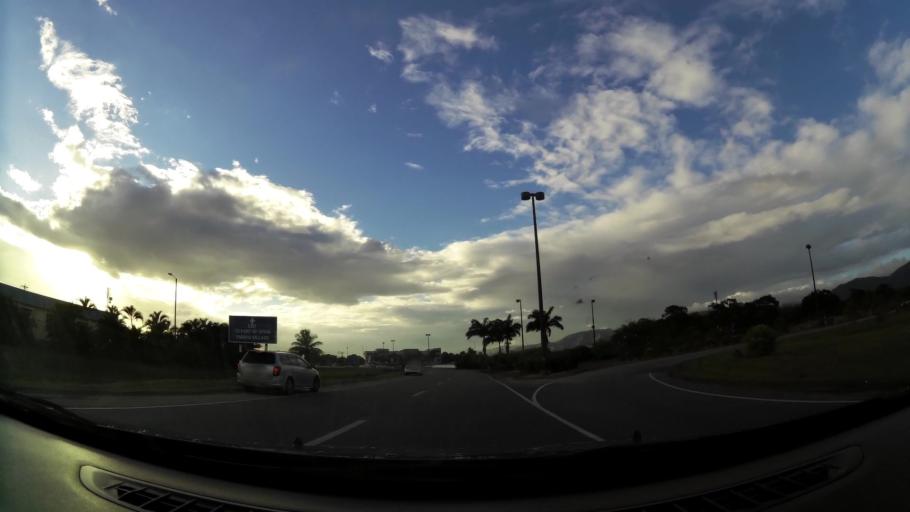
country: TT
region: Tunapuna/Piarco
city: Arouca
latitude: 10.6038
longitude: -61.3429
